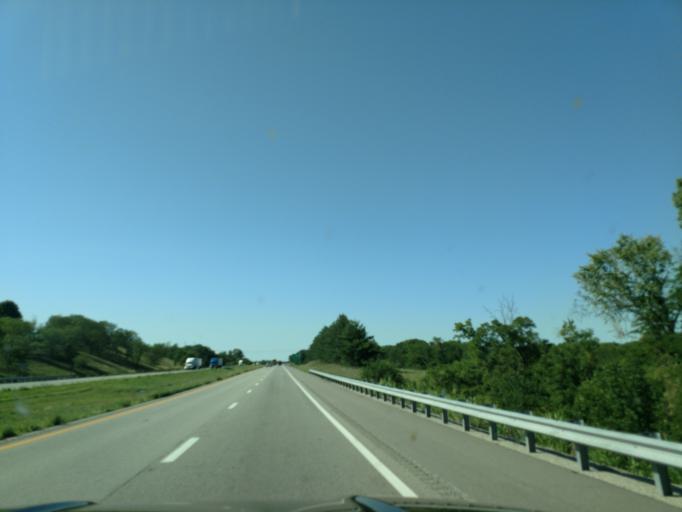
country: US
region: Missouri
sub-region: Andrew County
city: Country Club Village
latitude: 39.8383
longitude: -94.8052
